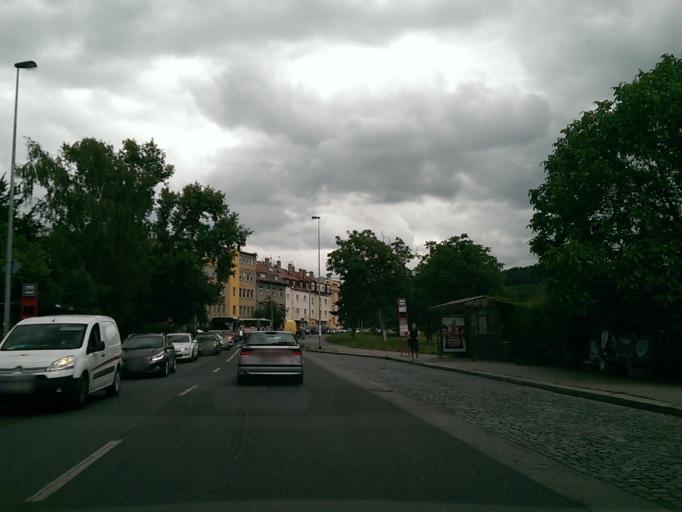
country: CZ
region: Praha
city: Branik
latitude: 50.0347
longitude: 14.4142
